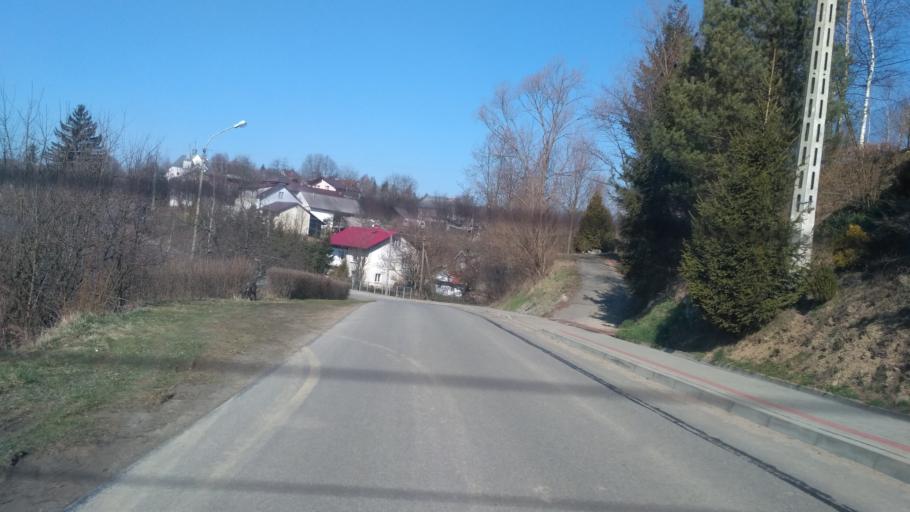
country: PL
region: Subcarpathian Voivodeship
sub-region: Powiat strzyzowski
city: Gwoznica Gorna
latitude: 49.8140
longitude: 22.0358
